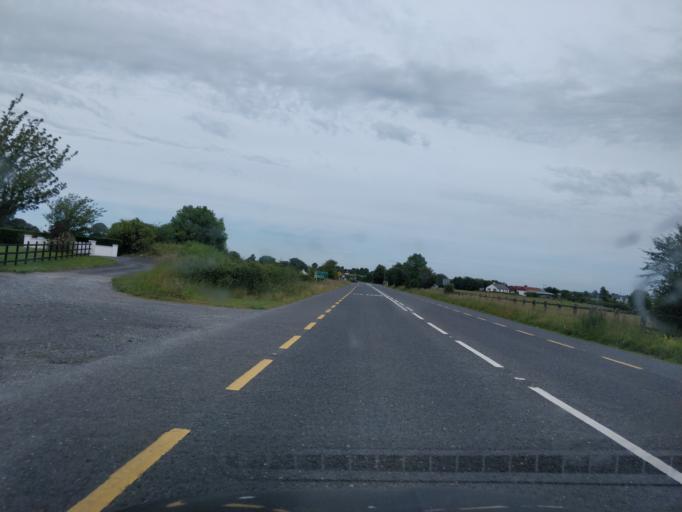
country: IE
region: Leinster
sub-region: Uibh Fhaili
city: Birr
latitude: 53.1496
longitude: -7.8397
